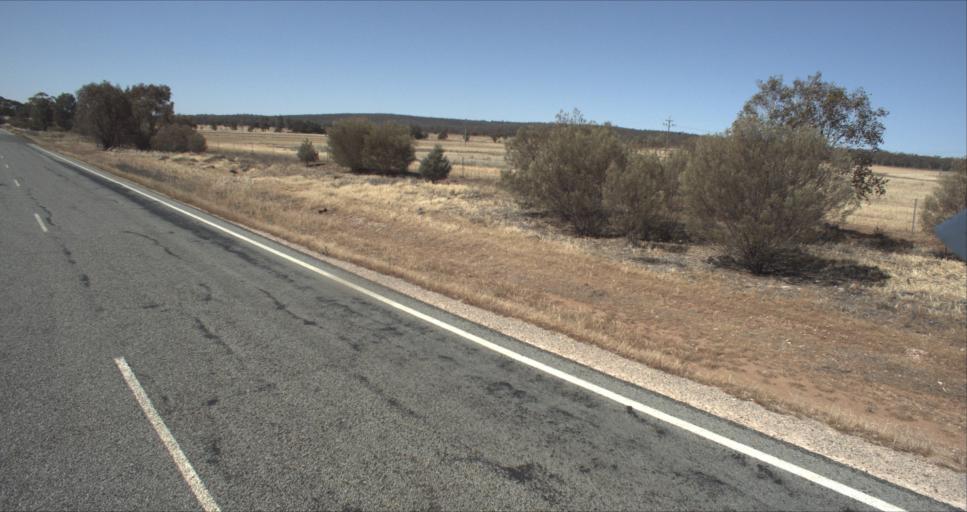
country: AU
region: New South Wales
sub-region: Leeton
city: Leeton
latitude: -34.4735
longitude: 146.4355
